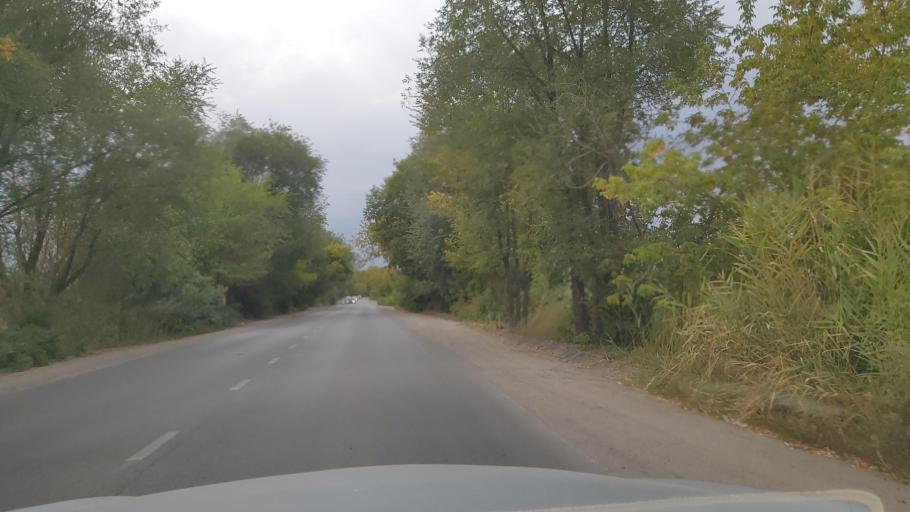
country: KZ
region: Almaty Oblysy
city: Energeticheskiy
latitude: 43.4032
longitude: 77.0318
